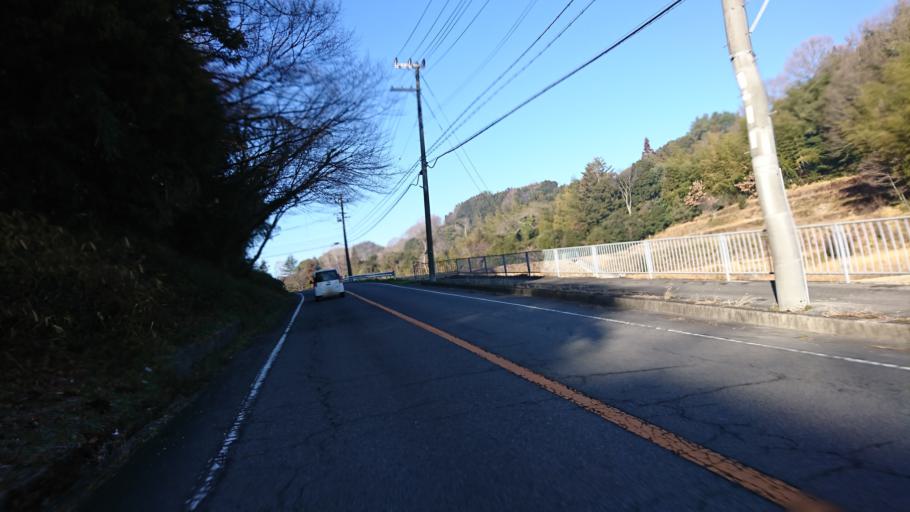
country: JP
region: Hyogo
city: Ono
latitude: 34.8421
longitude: 134.8589
